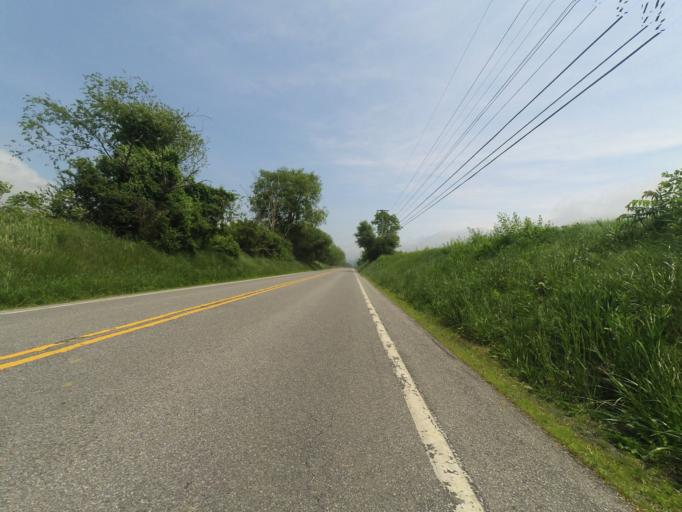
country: US
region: Pennsylvania
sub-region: Centre County
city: Stormstown
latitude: 40.7024
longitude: -77.9947
